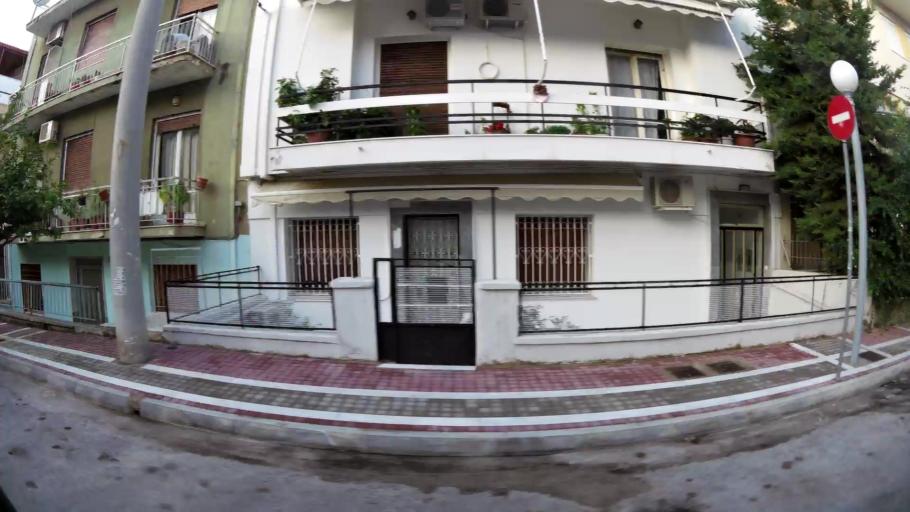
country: GR
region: Attica
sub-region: Nomarchia Athinas
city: Ymittos
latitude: 37.9500
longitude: 23.7472
